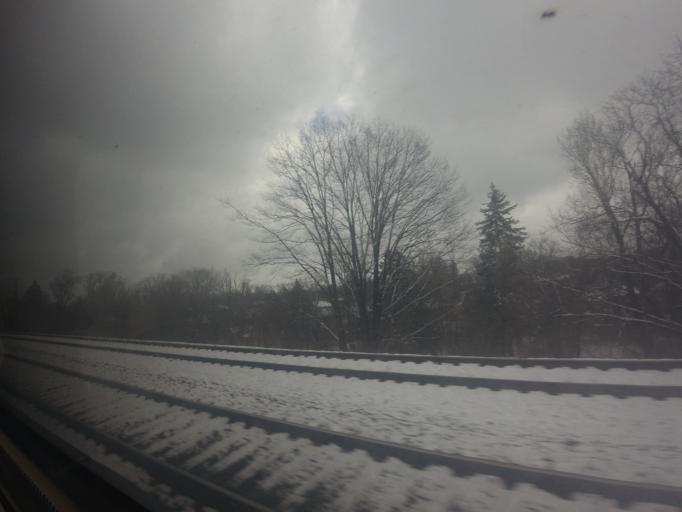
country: CA
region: Ontario
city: Scarborough
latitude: 43.6918
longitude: -79.2771
